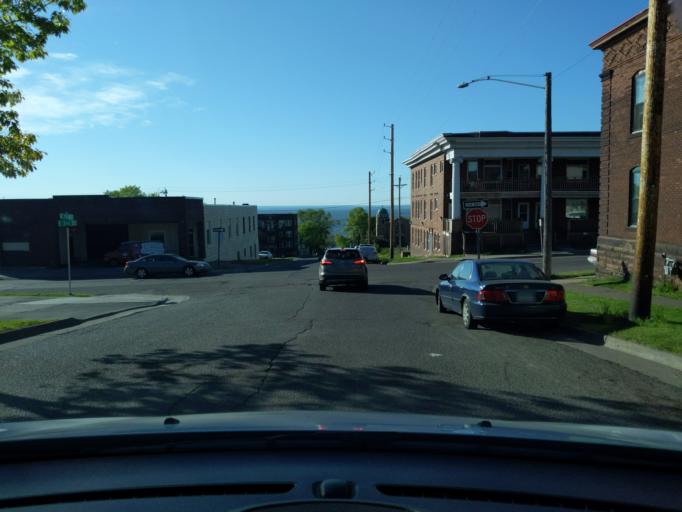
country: US
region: Minnesota
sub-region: Saint Louis County
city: Duluth
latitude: 46.7958
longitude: -92.0931
